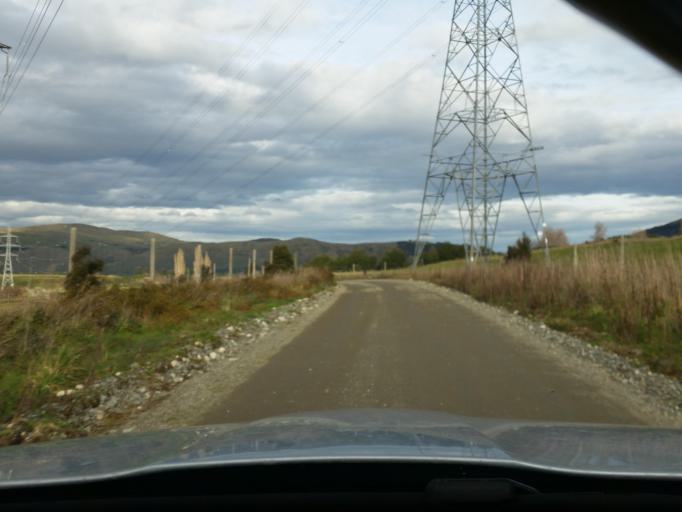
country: NZ
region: Southland
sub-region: Southland District
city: Te Anau
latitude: -45.8017
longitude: 167.6346
